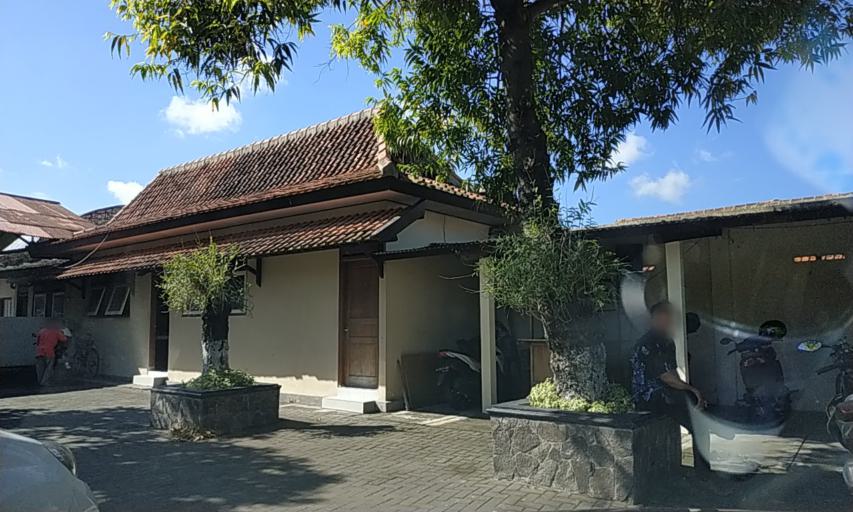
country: ID
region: Central Java
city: Klaten
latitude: -7.7038
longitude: 110.6000
